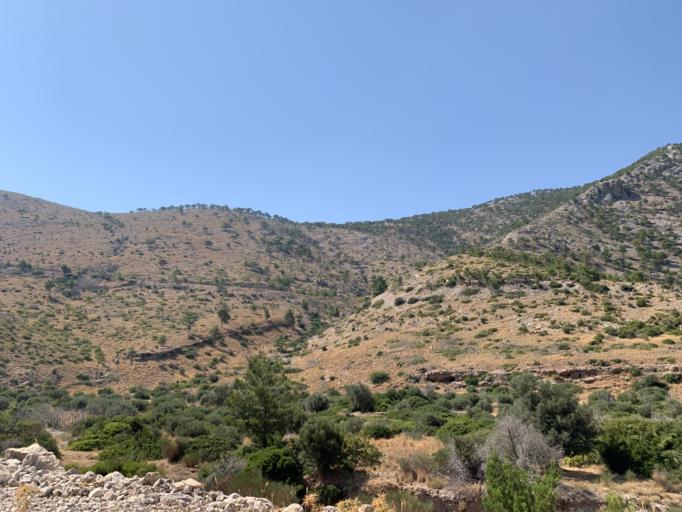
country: GR
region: North Aegean
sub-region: Chios
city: Vrontados
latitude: 38.3964
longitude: 25.9964
